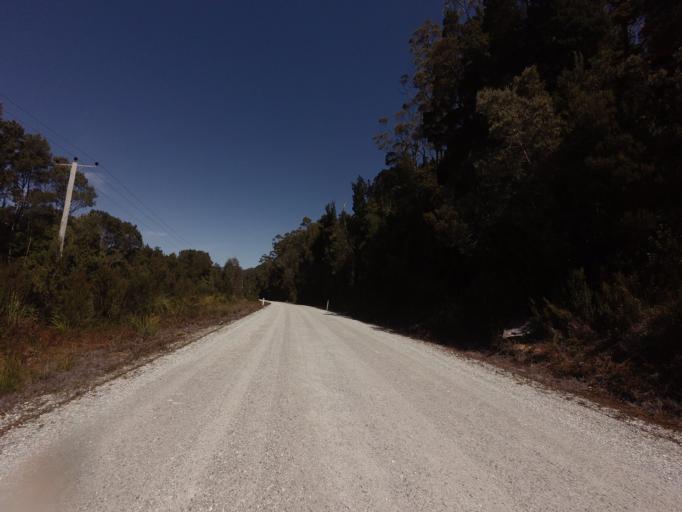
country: AU
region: Tasmania
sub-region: West Coast
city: Queenstown
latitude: -42.7588
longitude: 145.9853
